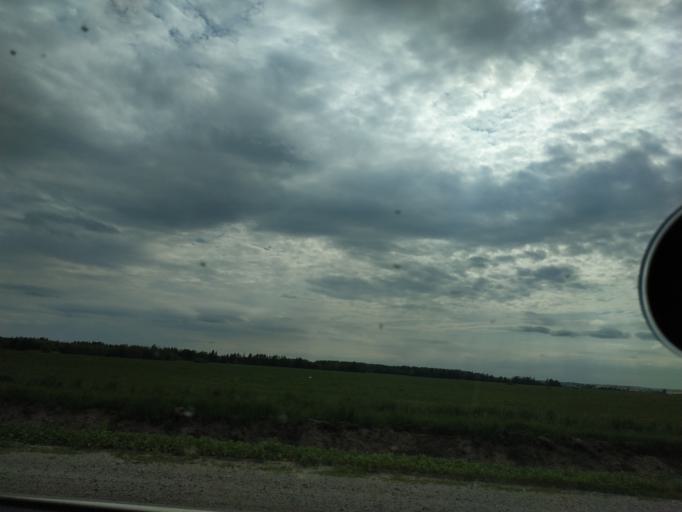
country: RU
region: Moskovskaya
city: Malyshevo
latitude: 55.5022
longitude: 38.2970
